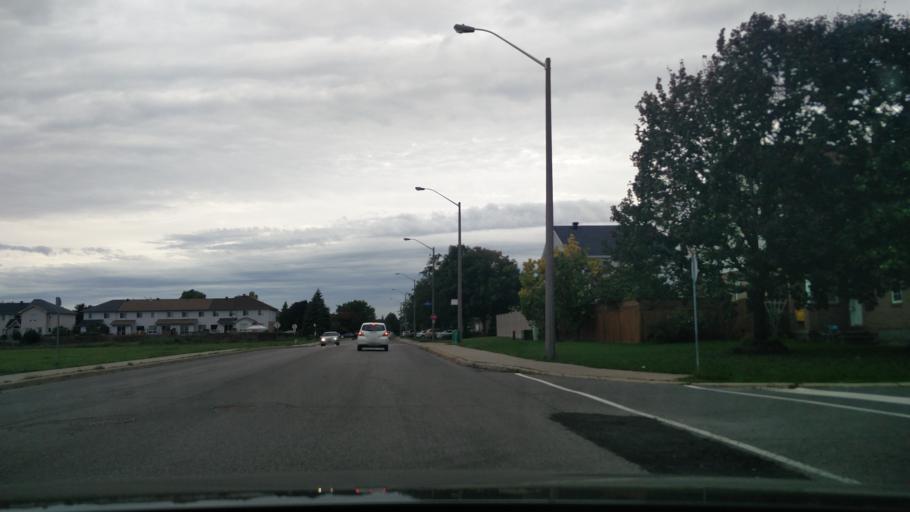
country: CA
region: Ontario
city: Bells Corners
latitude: 45.2916
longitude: -75.7378
